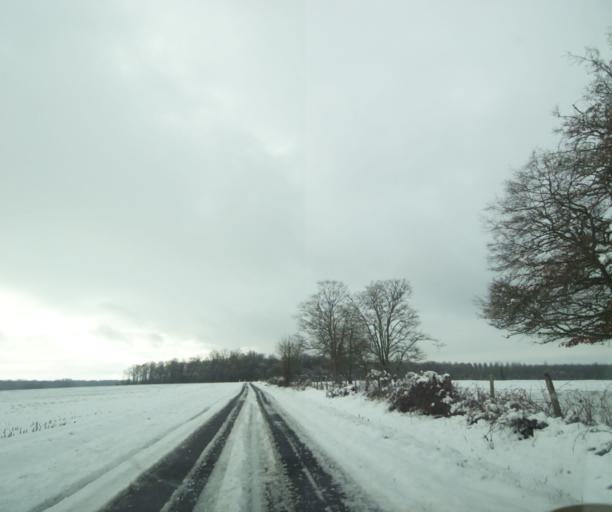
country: FR
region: Champagne-Ardenne
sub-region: Departement de la Haute-Marne
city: Montier-en-Der
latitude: 48.4863
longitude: 4.6851
